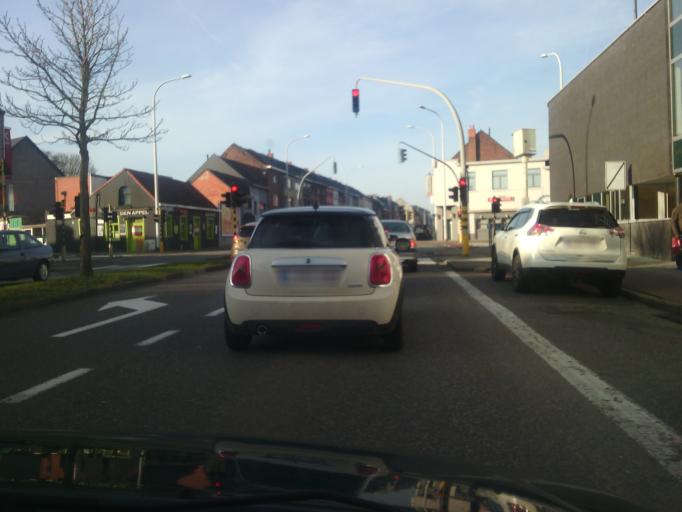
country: BE
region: Flanders
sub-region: Provincie Oost-Vlaanderen
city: Aalst
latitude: 50.9382
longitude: 4.0247
